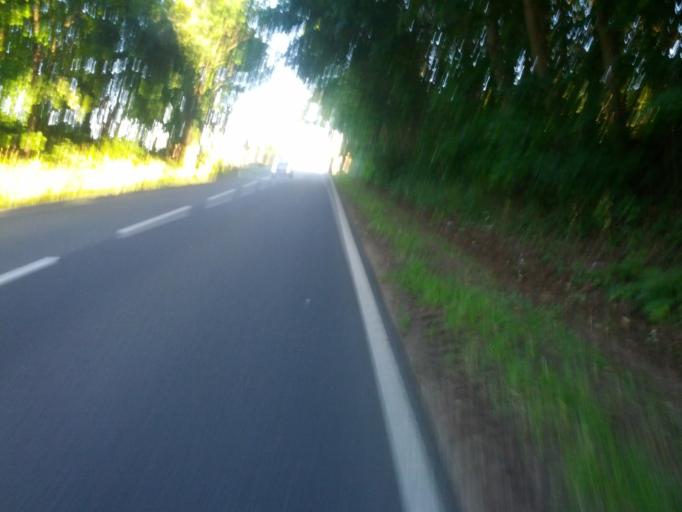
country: DE
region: Mecklenburg-Vorpommern
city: Bastorf
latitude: 54.1072
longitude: 11.6701
